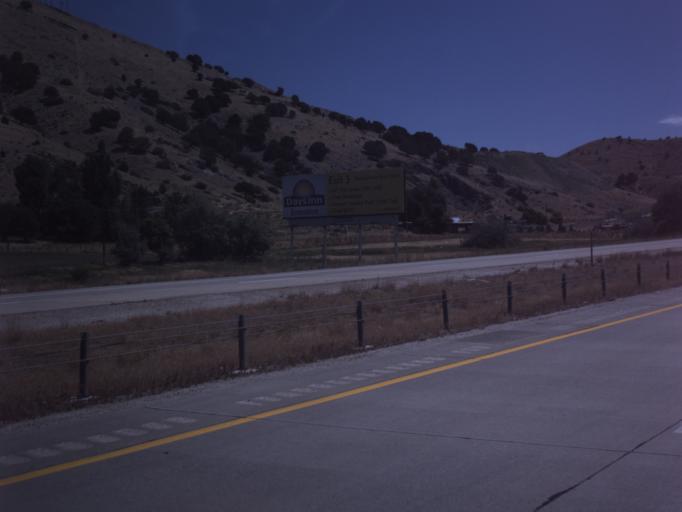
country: US
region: Utah
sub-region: Morgan County
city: Morgan
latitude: 41.0438
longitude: -111.6688
